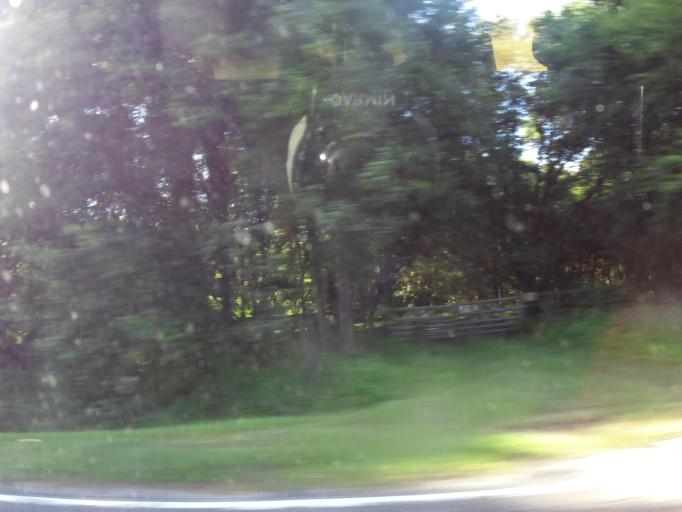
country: US
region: Florida
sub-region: Nassau County
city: Nassau Village-Ratliff
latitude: 30.4663
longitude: -81.8059
